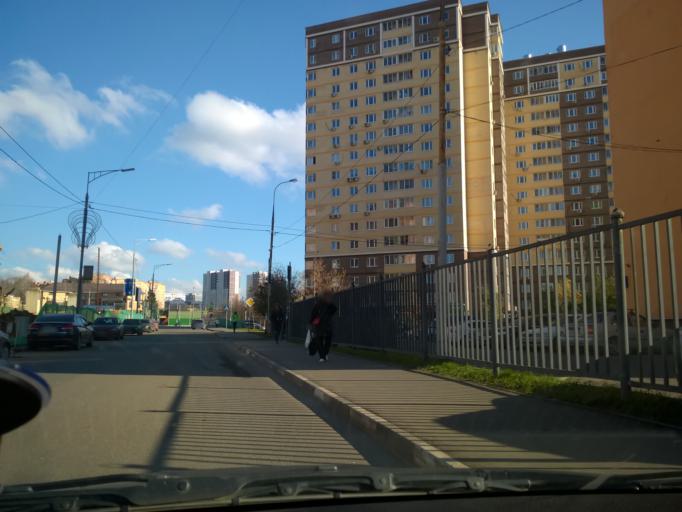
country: RU
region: Moskovskaya
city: Kommunarka
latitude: 55.5696
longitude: 37.4740
